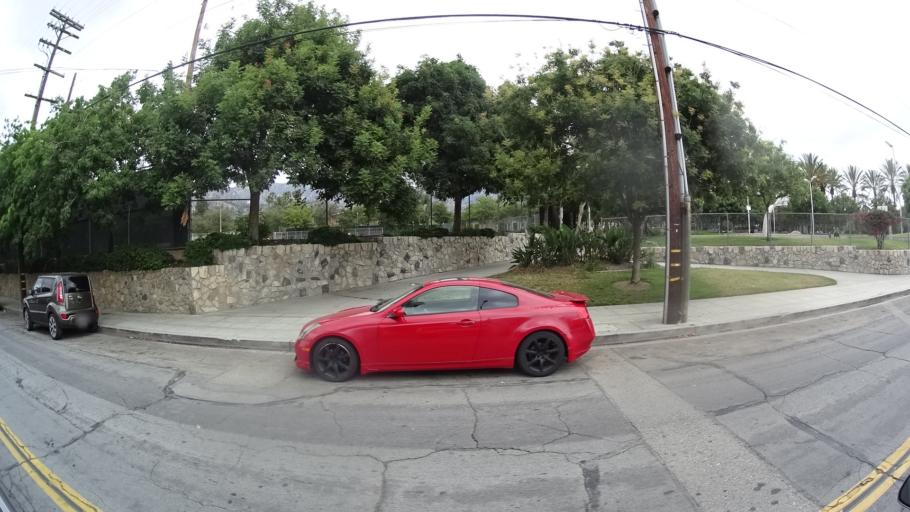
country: US
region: California
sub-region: Los Angeles County
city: Burbank
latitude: 34.1921
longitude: -118.3224
